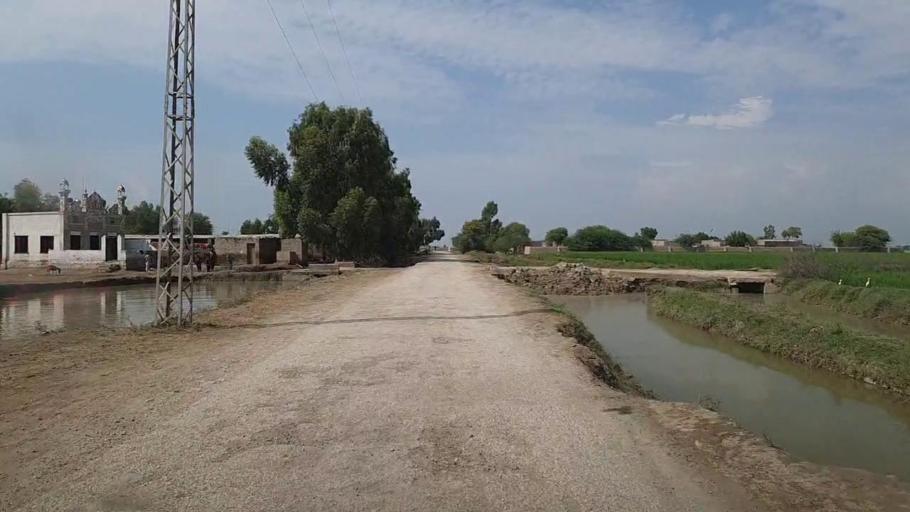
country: PK
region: Sindh
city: Thul
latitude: 28.2524
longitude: 68.8075
